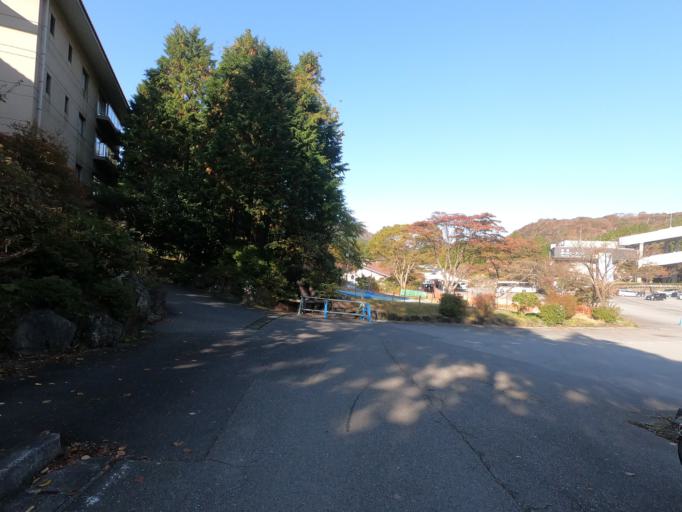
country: JP
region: Kanagawa
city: Hakone
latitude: 35.2119
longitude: 139.0111
